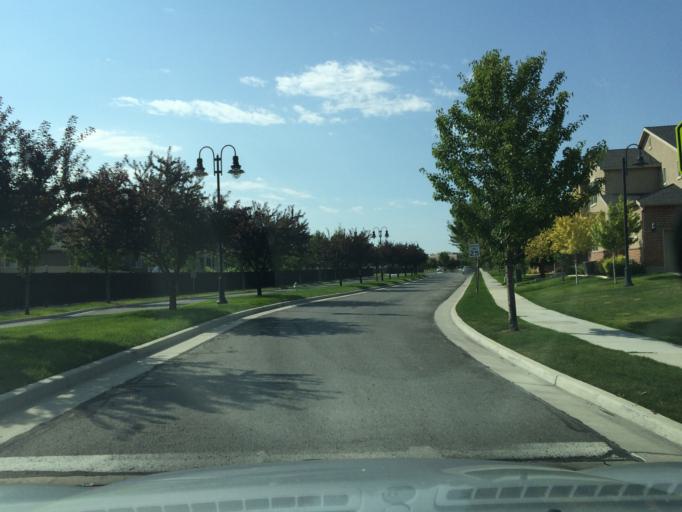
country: US
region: Utah
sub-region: Salt Lake County
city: West Valley City
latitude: 40.7079
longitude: -112.0203
